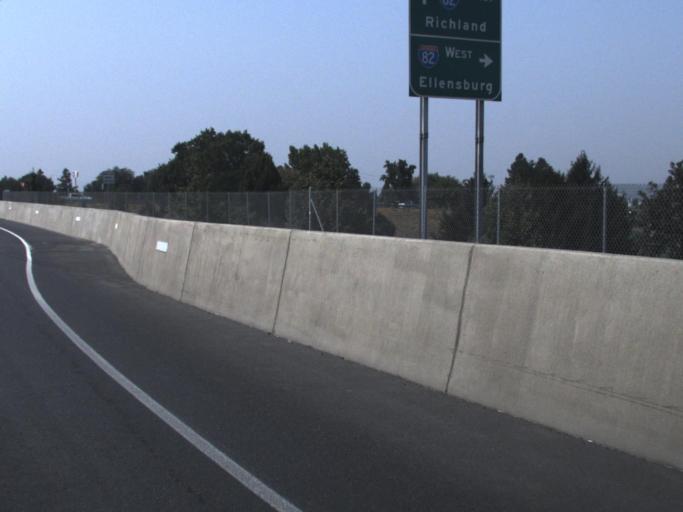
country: US
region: Washington
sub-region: Yakima County
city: Union Gap
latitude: 46.5850
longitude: -120.4696
